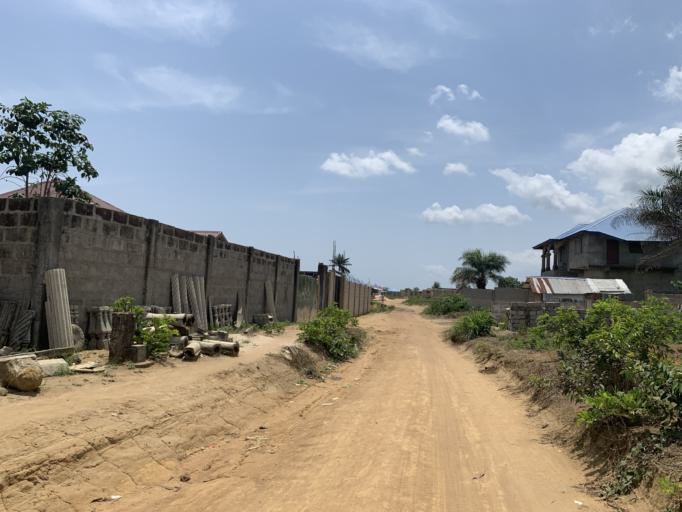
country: SL
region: Western Area
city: Waterloo
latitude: 8.3400
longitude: -13.0258
